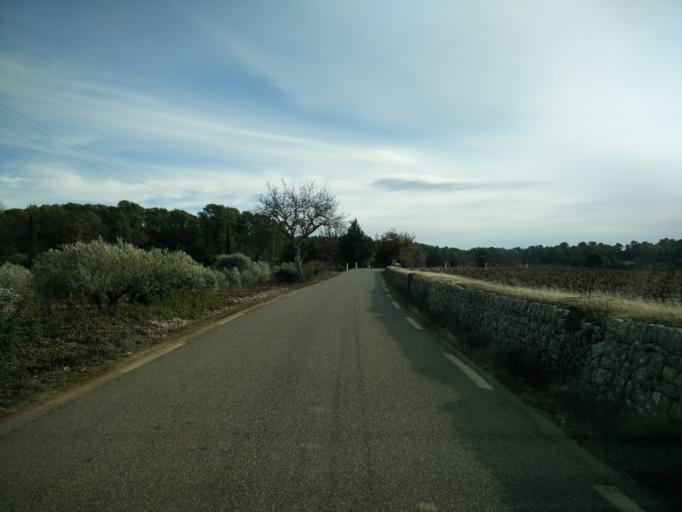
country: FR
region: Provence-Alpes-Cote d'Azur
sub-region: Departement du Var
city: Taradeau
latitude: 43.4645
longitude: 6.3900
